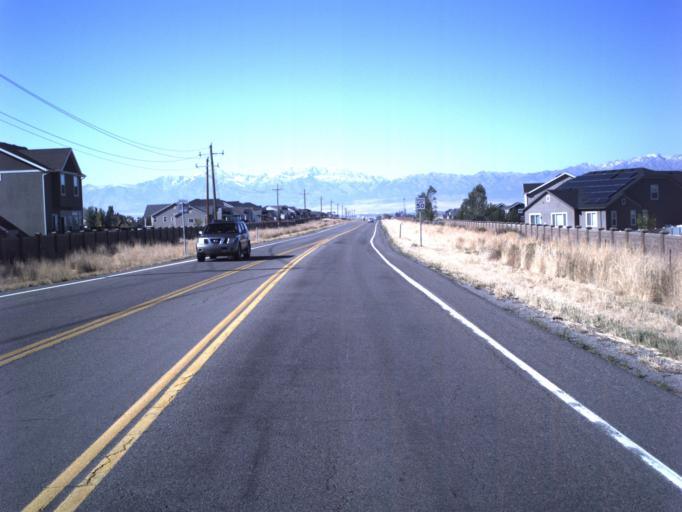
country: US
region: Utah
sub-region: Tooele County
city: Stansbury park
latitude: 40.6465
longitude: -112.3041
